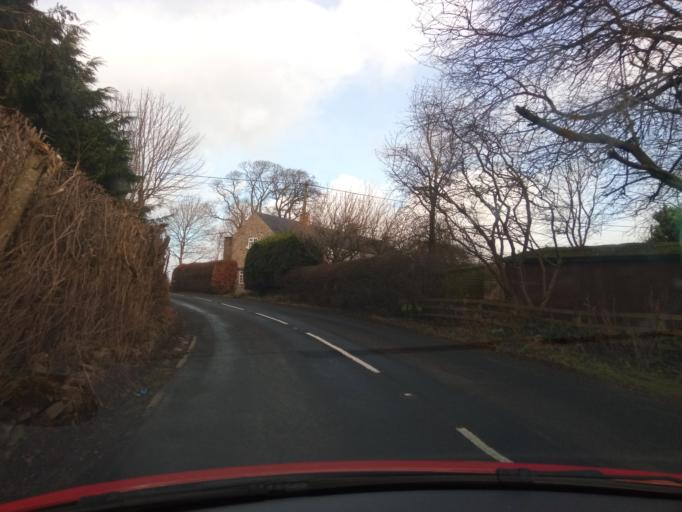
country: GB
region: England
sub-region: Northumberland
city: Corbridge
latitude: 55.1024
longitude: -2.0191
